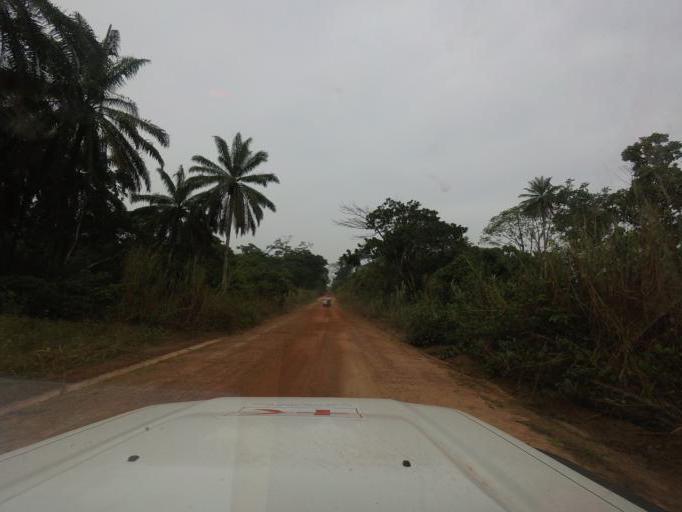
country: LR
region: Lofa
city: Voinjama
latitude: 8.3865
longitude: -9.8249
